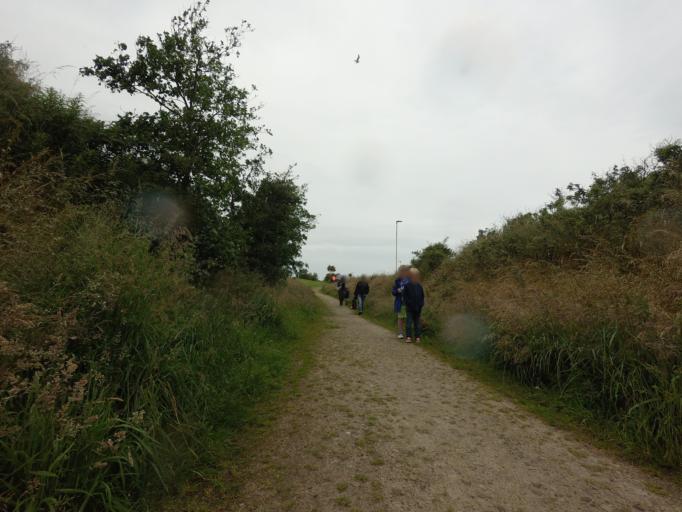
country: GB
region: Scotland
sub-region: Moray
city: Portknockie
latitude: 57.7013
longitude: -2.8552
